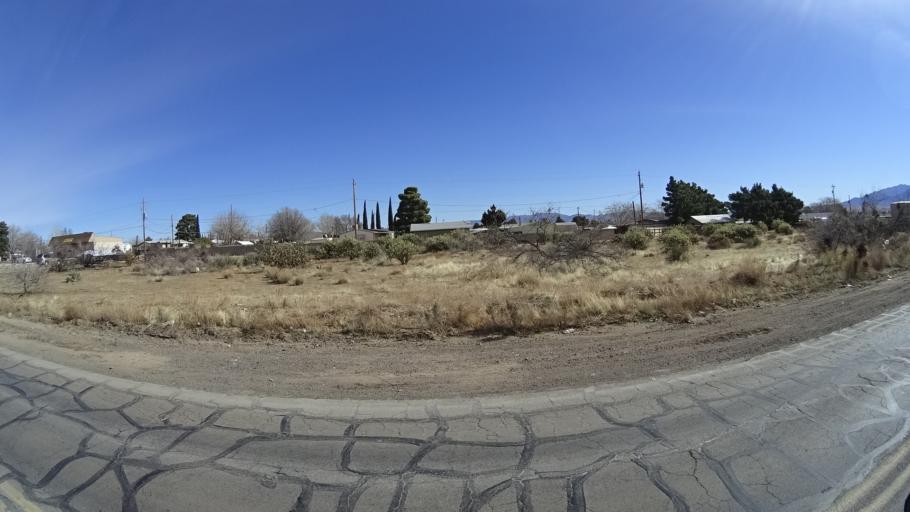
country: US
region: Arizona
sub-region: Mohave County
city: New Kingman-Butler
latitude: 35.2672
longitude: -114.0426
